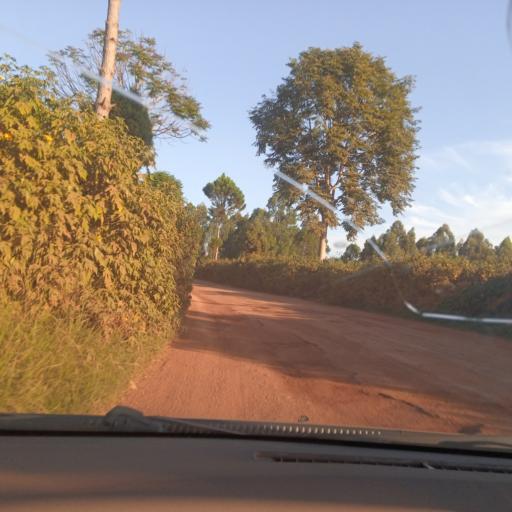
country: UG
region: Central Region
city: Masaka
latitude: -0.3329
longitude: 31.7583
